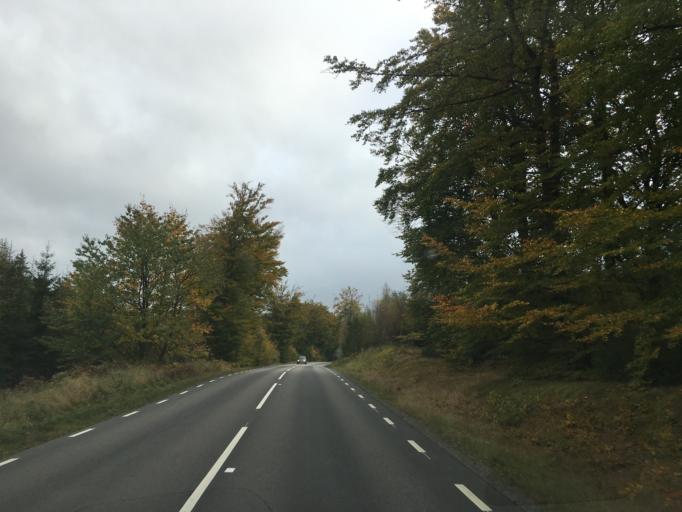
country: SE
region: Skane
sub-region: Tomelilla Kommun
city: Tomelilla
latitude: 55.6353
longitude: 14.0860
